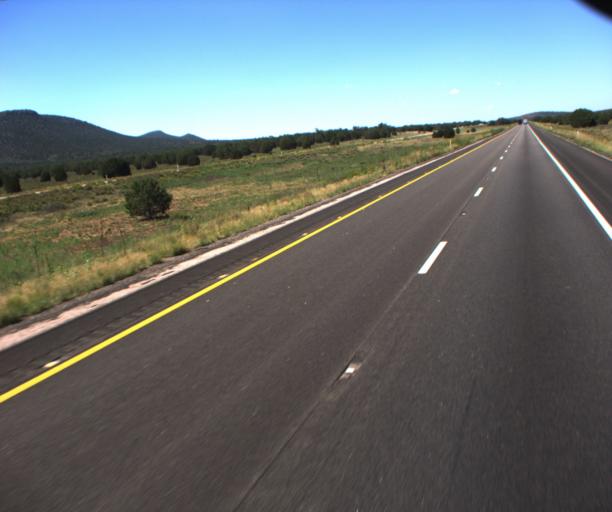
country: US
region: Arizona
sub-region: Mohave County
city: Peach Springs
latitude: 35.2190
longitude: -113.2497
